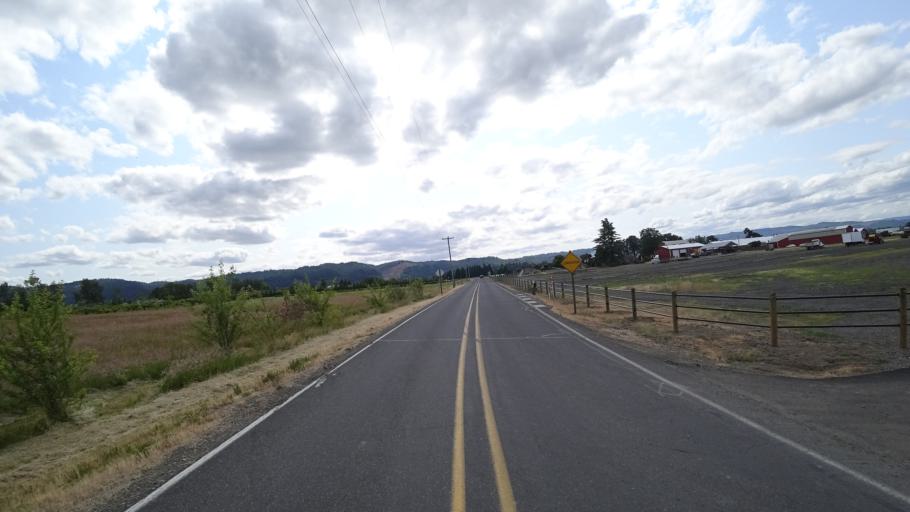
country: US
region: Washington
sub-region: Clark County
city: Felida
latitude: 45.6419
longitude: -122.7868
